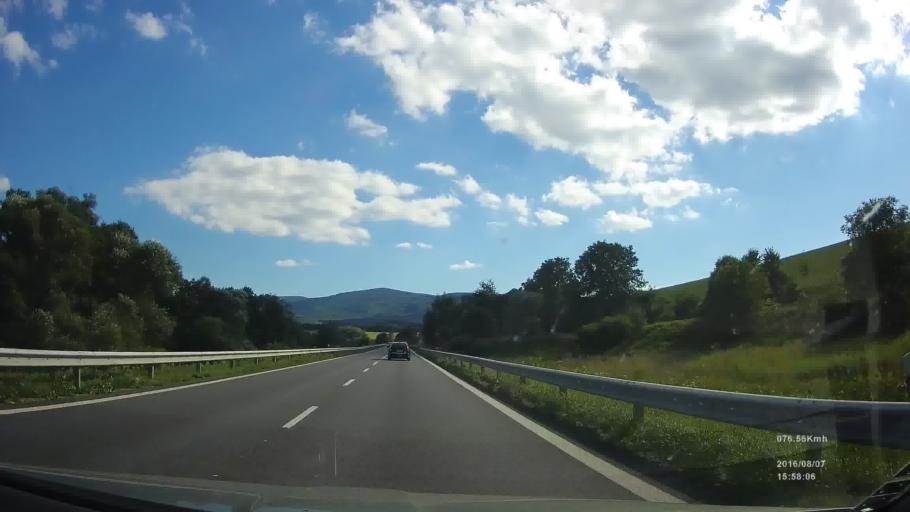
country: SK
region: Presovsky
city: Giraltovce
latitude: 49.0527
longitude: 21.4170
